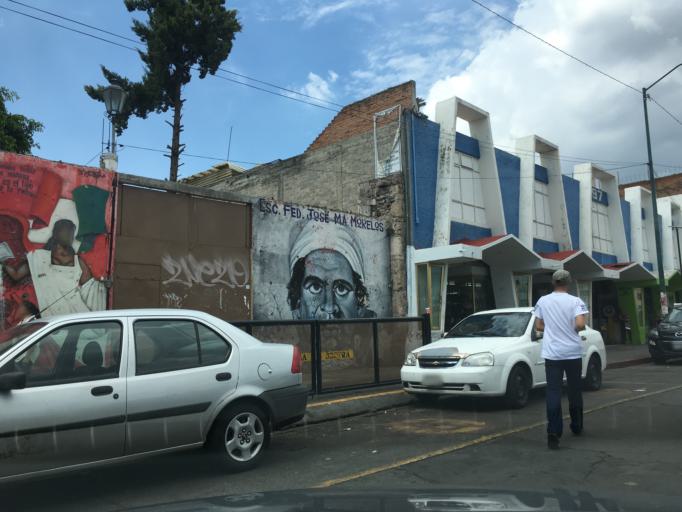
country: MX
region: Michoacan
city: Morelia
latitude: 19.6971
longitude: -101.1887
